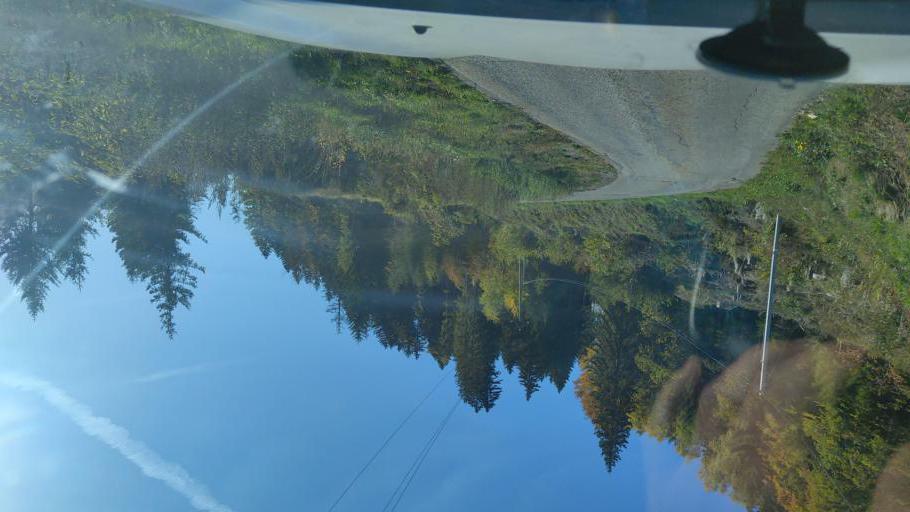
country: FR
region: Rhone-Alpes
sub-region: Departement de la Savoie
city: Beaufort
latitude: 45.7268
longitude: 6.5025
